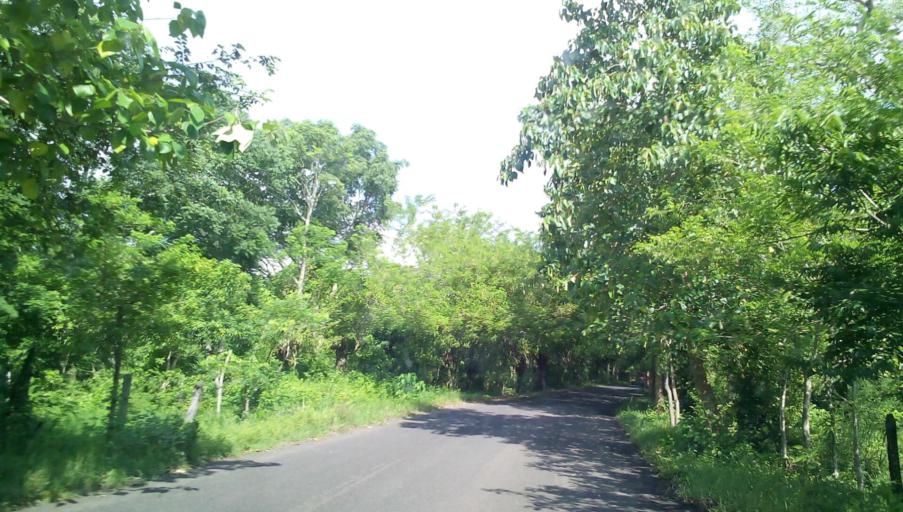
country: MX
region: Veracruz
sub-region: Citlaltepetl
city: Las Sabinas
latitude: 21.3529
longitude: -97.8971
